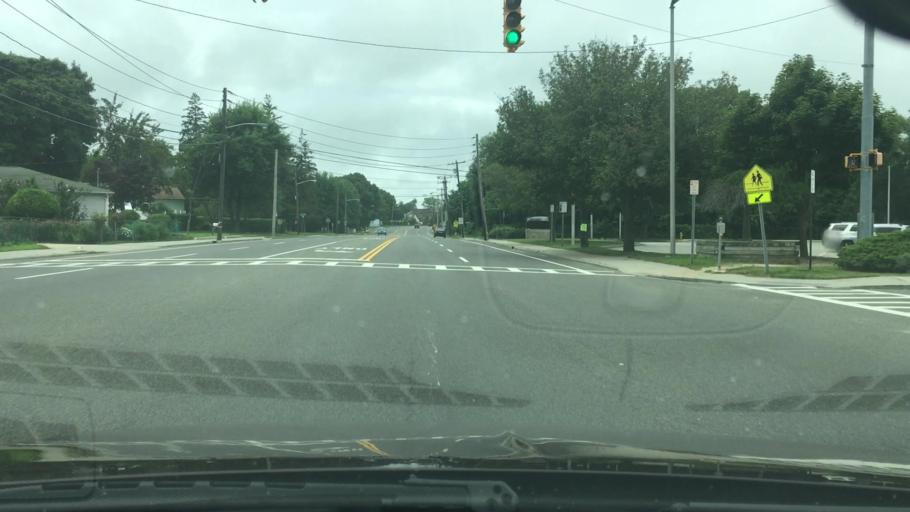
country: US
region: New York
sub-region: Suffolk County
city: Copiague
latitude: 40.6891
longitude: -73.3958
